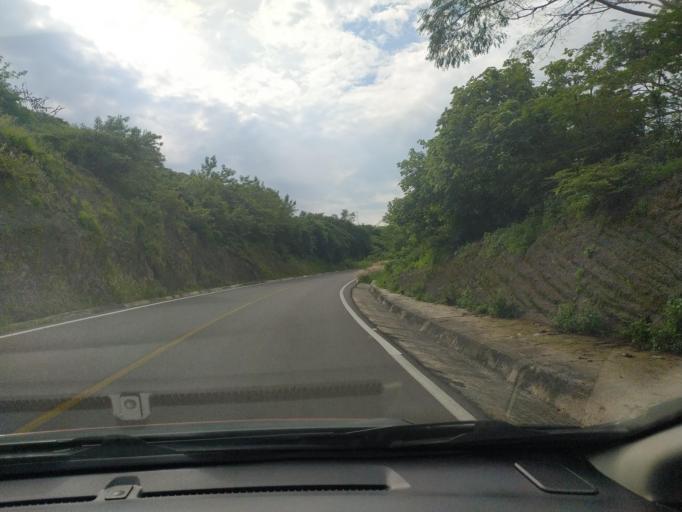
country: MX
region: Jalisco
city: Villa Corona
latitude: 20.3938
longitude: -103.6772
